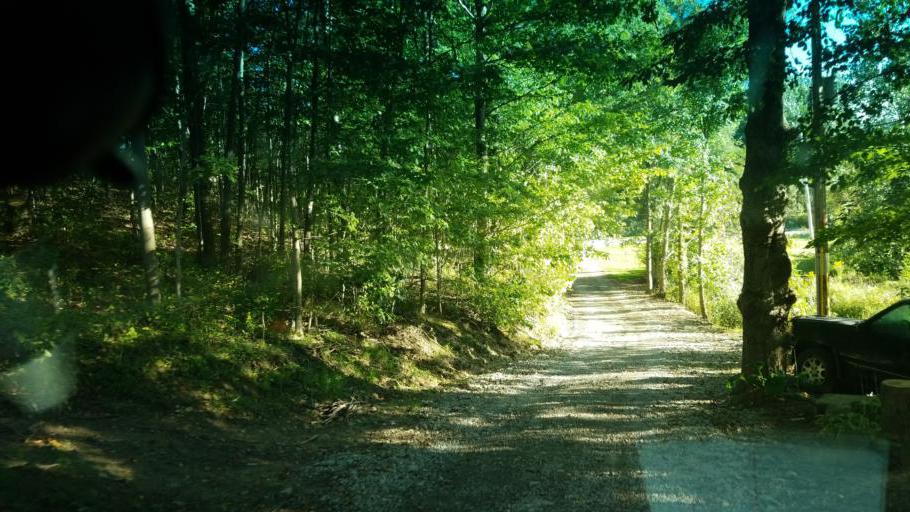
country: US
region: Ohio
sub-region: Richland County
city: Lexington
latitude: 40.6531
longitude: -82.6874
